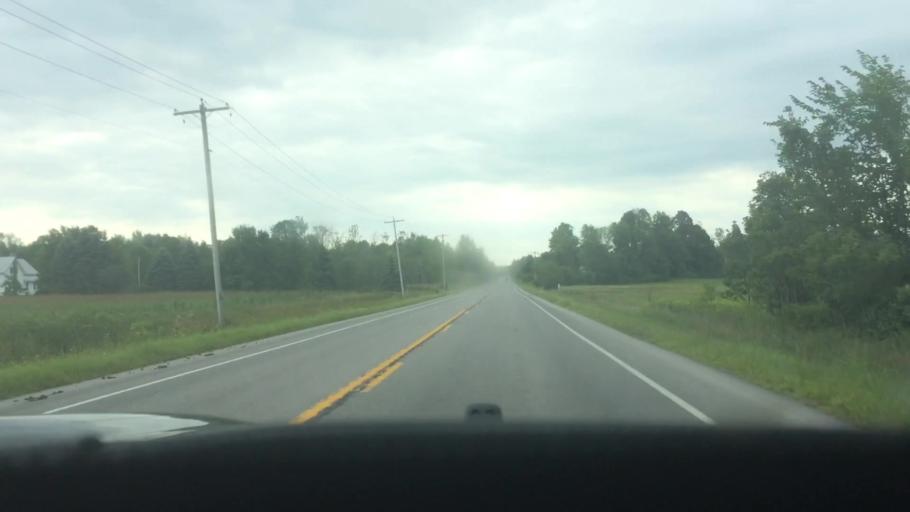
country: US
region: New York
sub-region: St. Lawrence County
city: Ogdensburg
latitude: 44.6058
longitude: -75.3928
